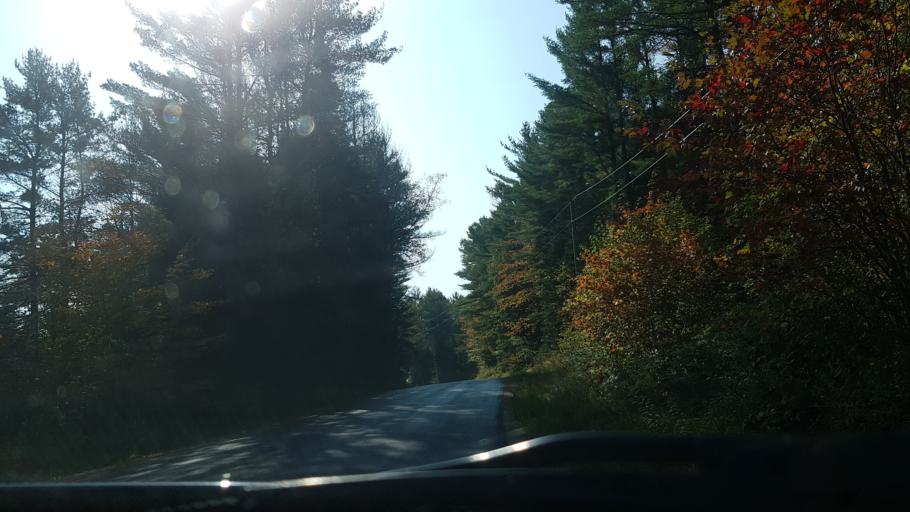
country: CA
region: Ontario
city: Bracebridge
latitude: 44.9673
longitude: -79.2548
